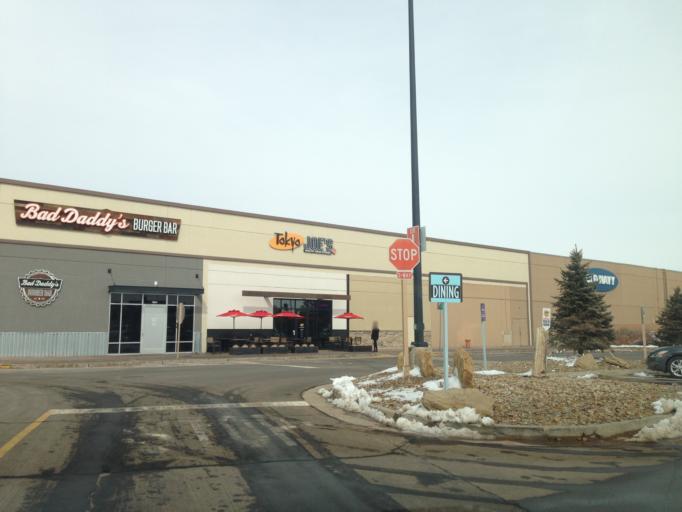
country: US
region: Colorado
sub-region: Boulder County
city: Superior
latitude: 39.9317
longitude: -105.1336
